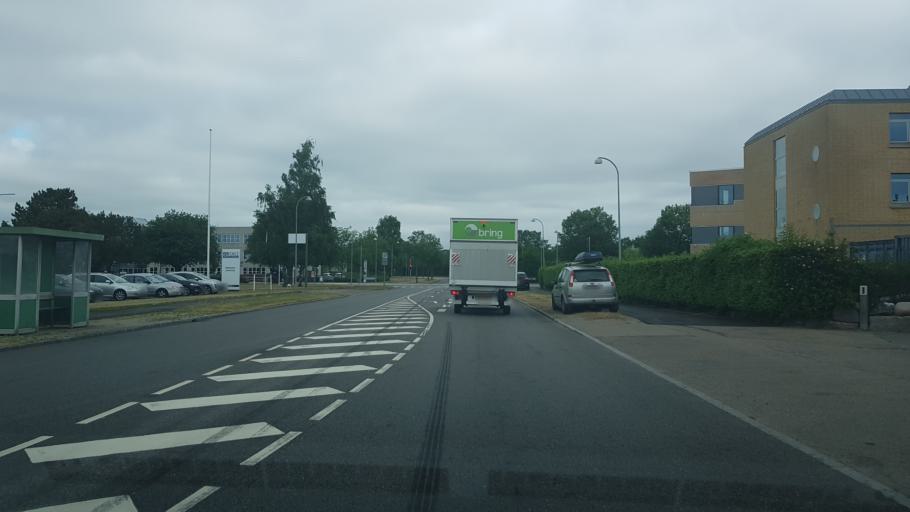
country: DK
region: Capital Region
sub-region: Albertslund Kommune
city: Albertslund
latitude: 55.6510
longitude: 12.3852
